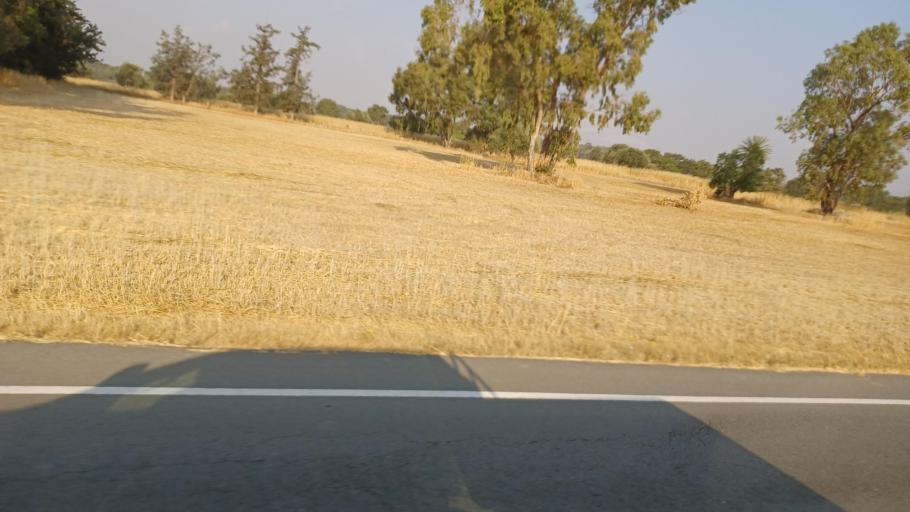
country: CY
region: Larnaka
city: Tersefanou
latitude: 34.8294
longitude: 33.5107
